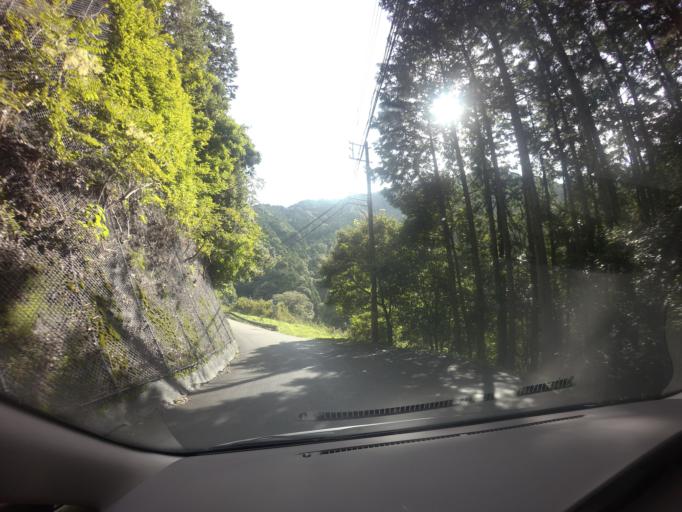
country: JP
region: Wakayama
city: Shingu
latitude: 33.9662
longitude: 135.8448
